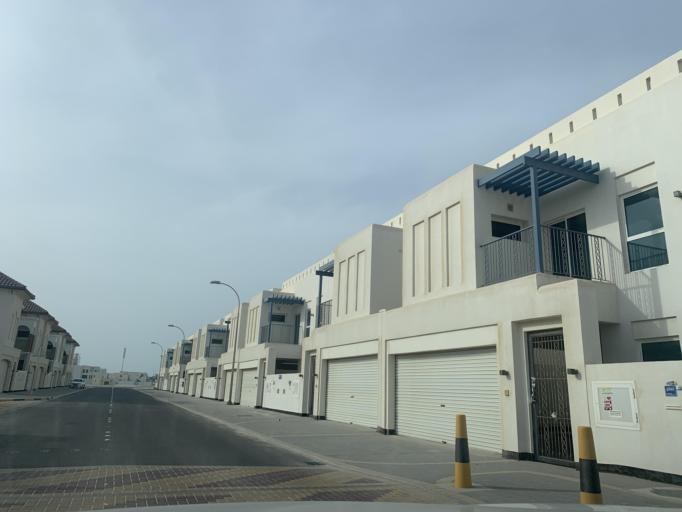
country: BH
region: Muharraq
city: Al Muharraq
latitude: 26.3177
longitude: 50.6280
